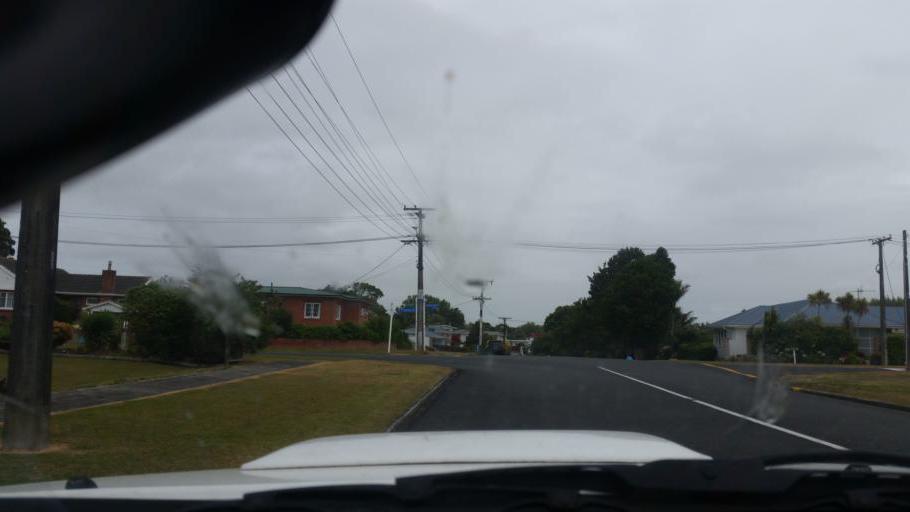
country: NZ
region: Northland
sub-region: Kaipara District
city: Dargaville
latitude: -35.9344
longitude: 173.8643
